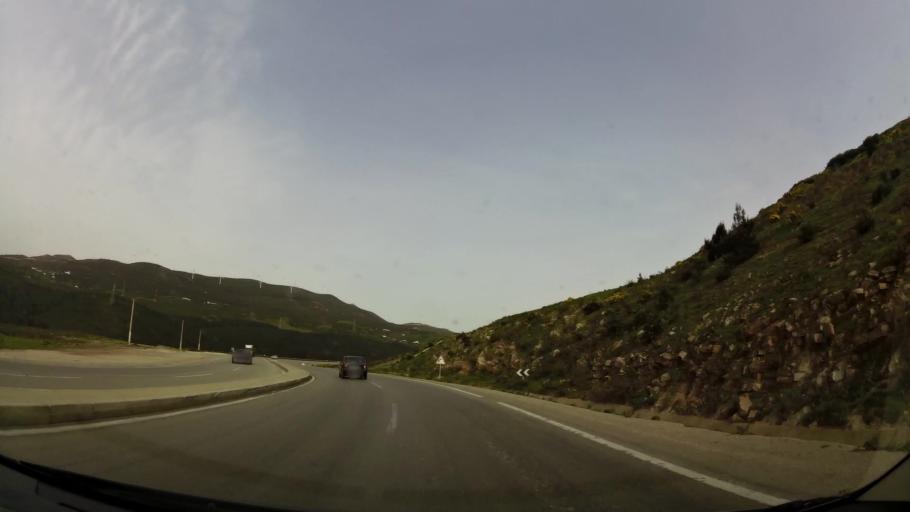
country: MA
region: Tanger-Tetouan
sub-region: Tanger-Assilah
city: Dar Chaoui
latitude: 35.5653
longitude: -5.5882
